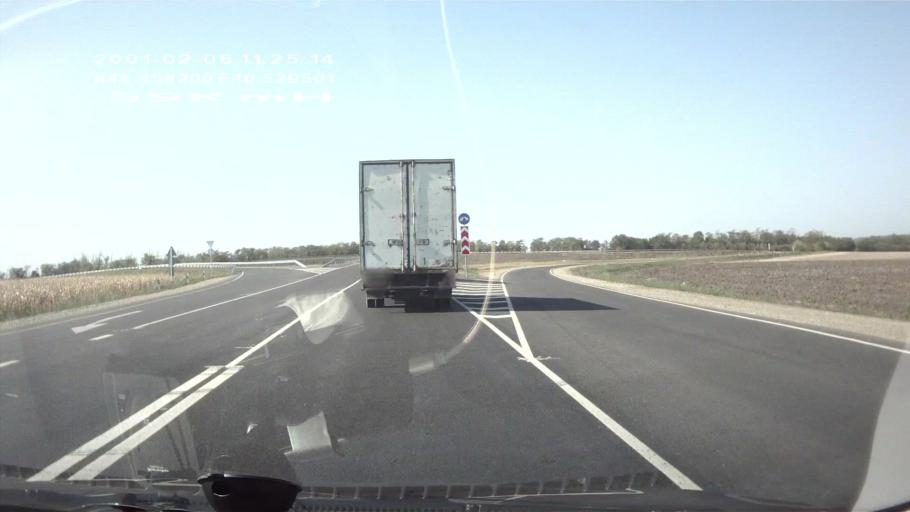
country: RU
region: Krasnodarskiy
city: Kropotkin
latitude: 45.4581
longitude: 40.5288
